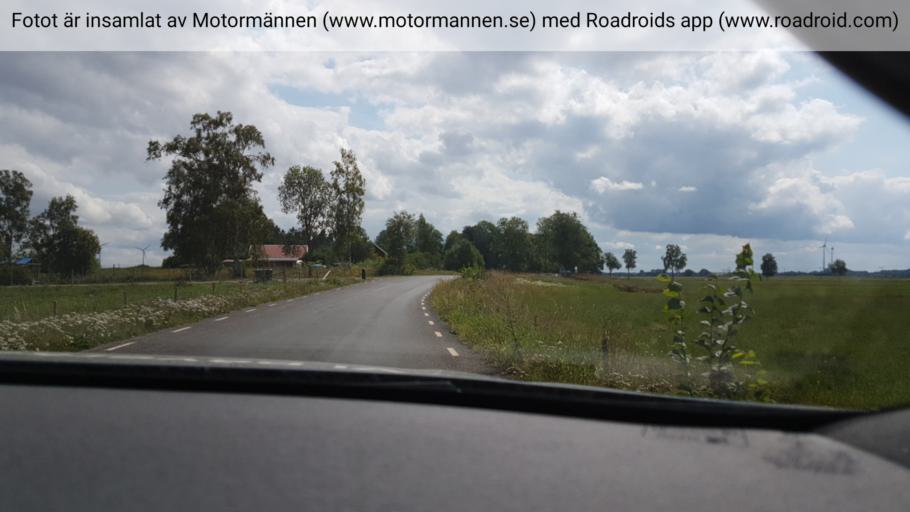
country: SE
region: Vaestra Goetaland
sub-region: Falkopings Kommun
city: Falkoeping
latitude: 58.1042
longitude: 13.4764
